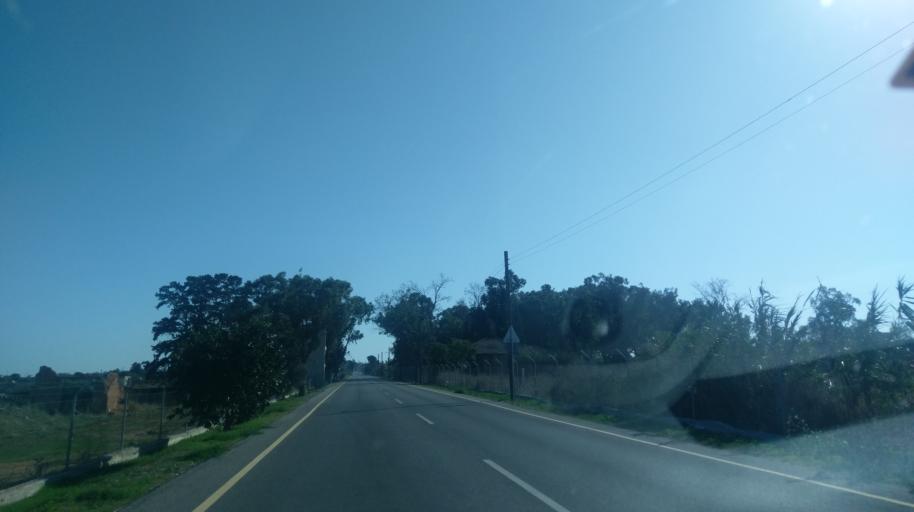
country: CY
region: Ammochostos
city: Deryneia
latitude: 35.0828
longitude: 33.9565
